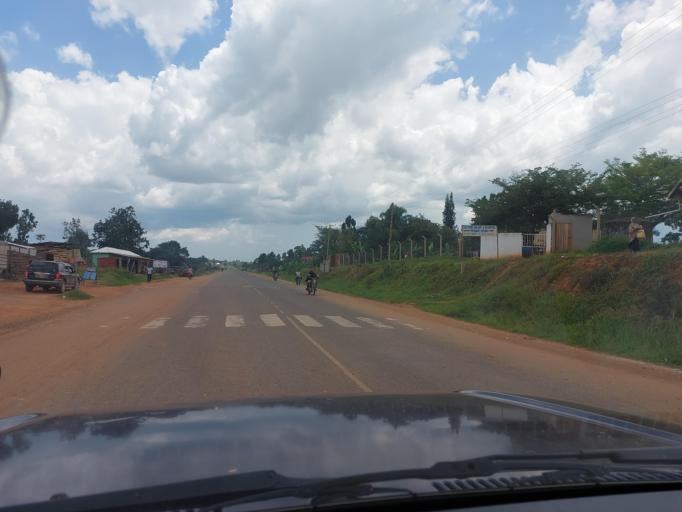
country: UG
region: Central Region
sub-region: Mukono District
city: Mukono
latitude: 0.3156
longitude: 32.7704
